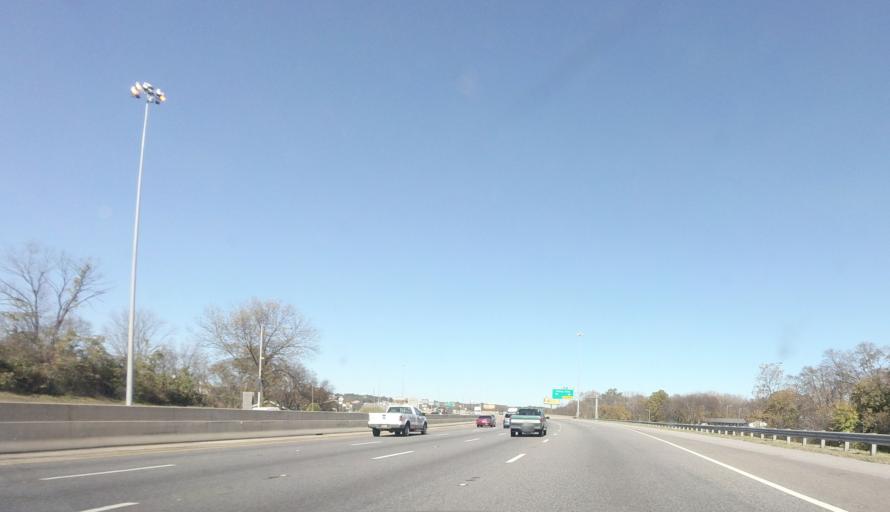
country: US
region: Alabama
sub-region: Jefferson County
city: Birmingham
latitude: 33.5346
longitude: -86.8236
